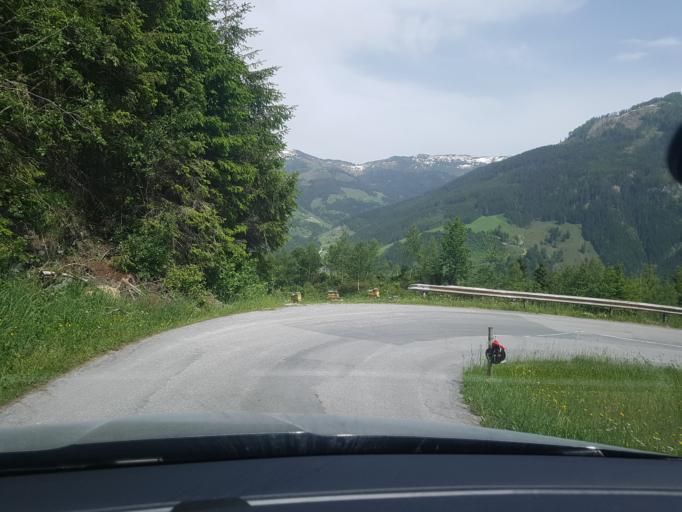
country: AT
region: Salzburg
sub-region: Politischer Bezirk Sankt Johann im Pongau
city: Schwarzach im Pongau
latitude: 47.2759
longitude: 13.1984
